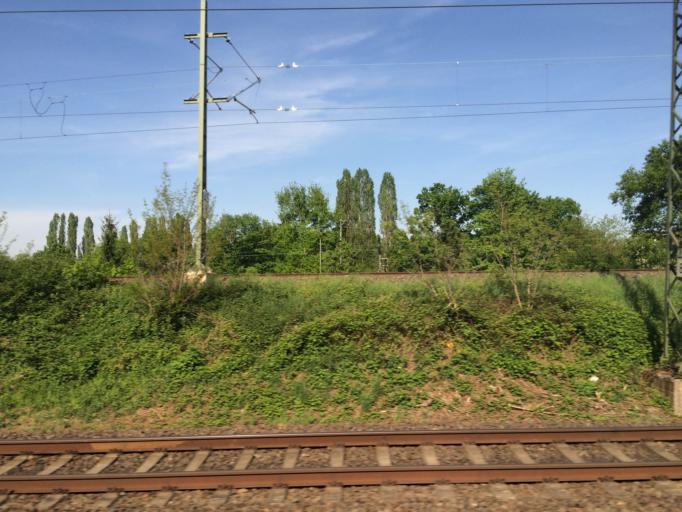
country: DE
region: North Rhine-Westphalia
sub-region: Regierungsbezirk Koln
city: Muelheim
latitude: 50.9763
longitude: 7.0142
